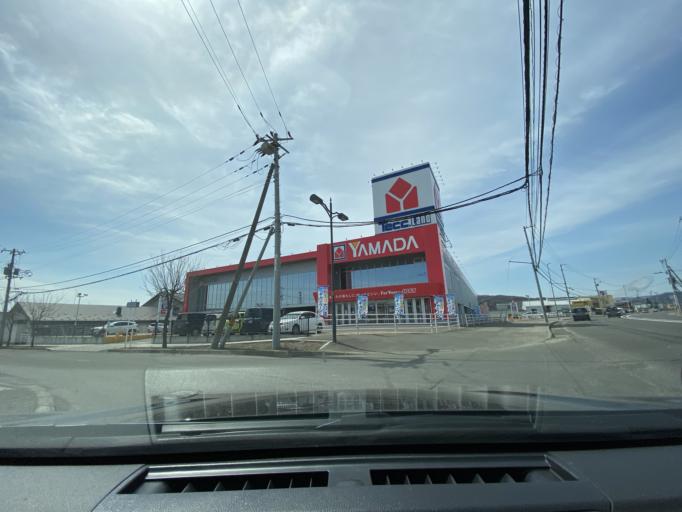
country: JP
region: Hokkaido
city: Kitami
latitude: 43.7967
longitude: 143.8392
